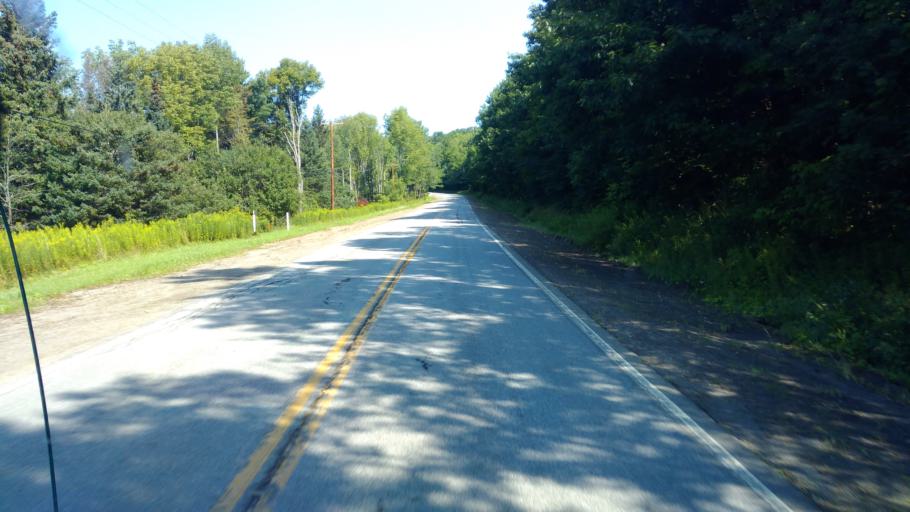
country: US
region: New York
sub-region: Allegany County
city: Bolivar
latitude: 42.1084
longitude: -78.1768
